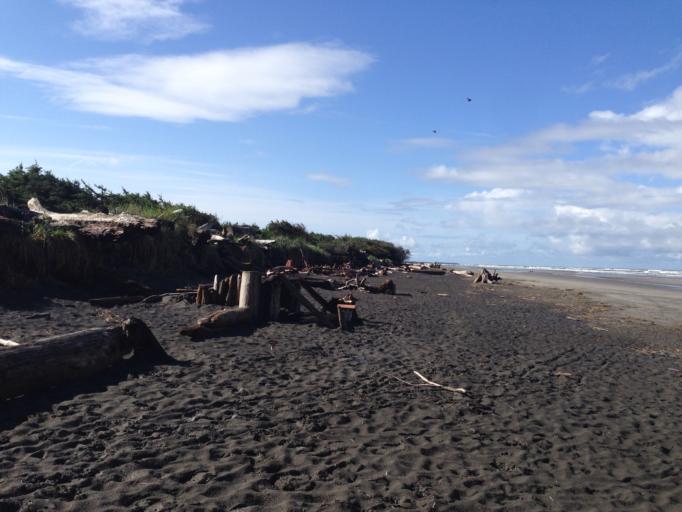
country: US
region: Washington
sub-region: Pacific County
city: Long Beach
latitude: 46.2949
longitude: -124.0755
